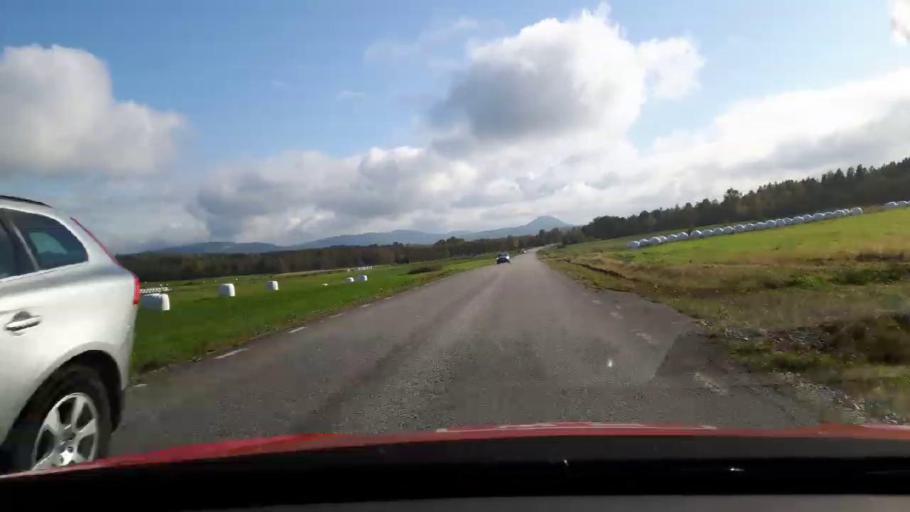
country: SE
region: Gaevleborg
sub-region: Ljusdals Kommun
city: Ljusdal
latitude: 61.7611
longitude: 16.0847
